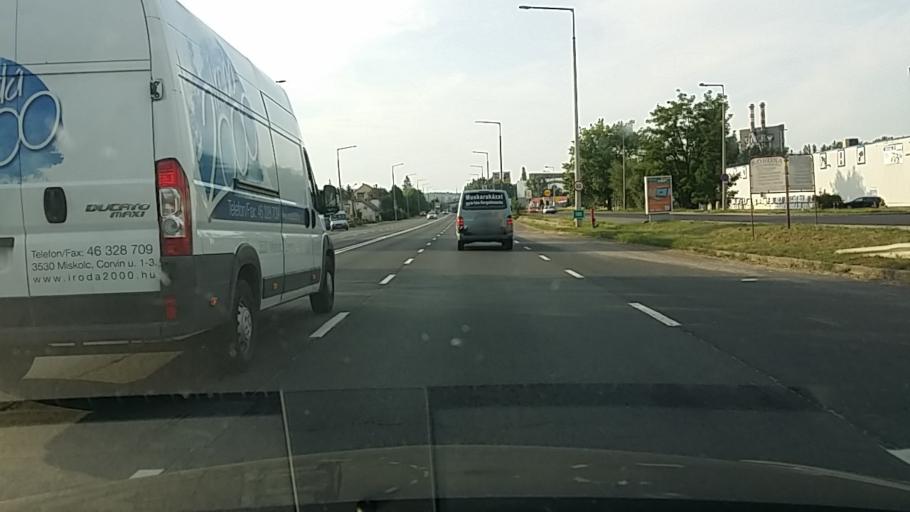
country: HU
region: Borsod-Abauj-Zemplen
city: Miskolc
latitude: 48.0572
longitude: 20.7971
